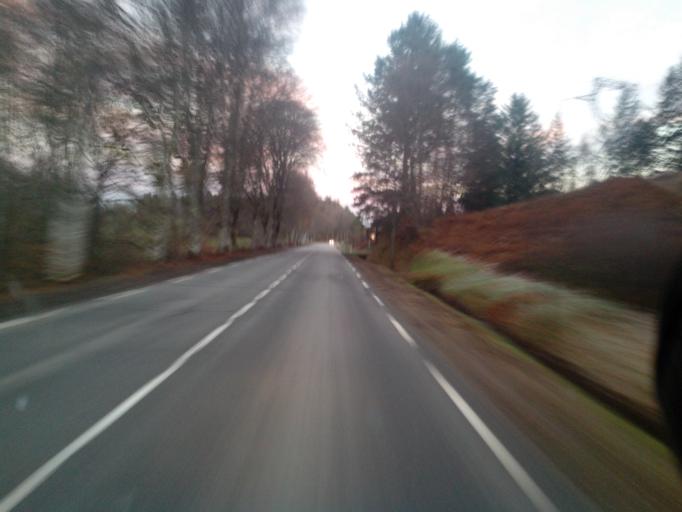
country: FR
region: Limousin
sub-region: Departement de la Correze
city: Meymac
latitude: 45.5143
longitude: 2.1815
